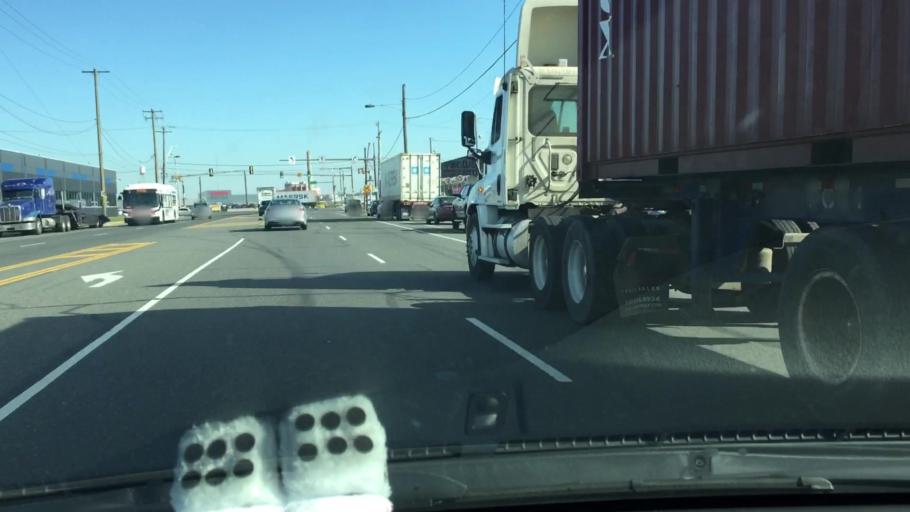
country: US
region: New Jersey
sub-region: Camden County
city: Camden
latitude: 39.9127
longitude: -75.1401
